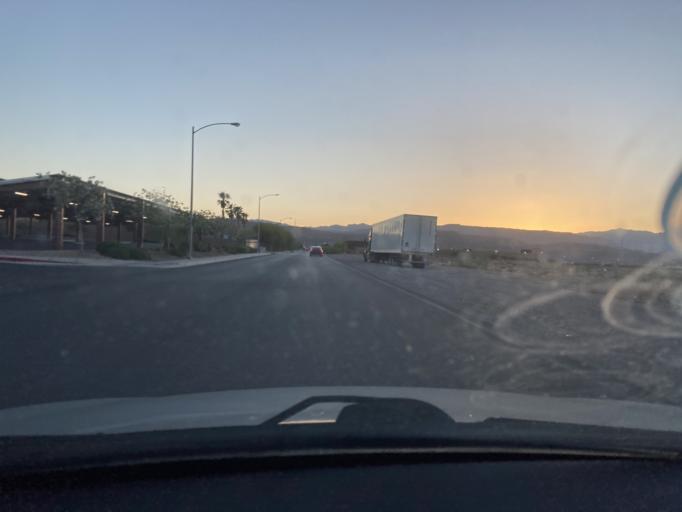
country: US
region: Nevada
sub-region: Clark County
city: Enterprise
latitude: 36.0593
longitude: -115.2721
